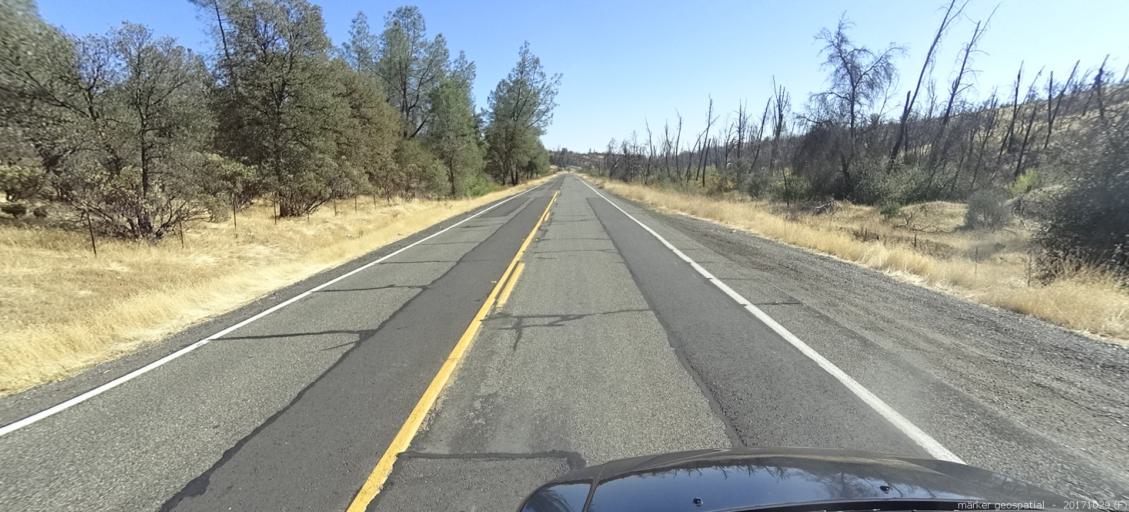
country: US
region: California
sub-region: Shasta County
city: Shasta
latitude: 40.4906
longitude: -122.5267
